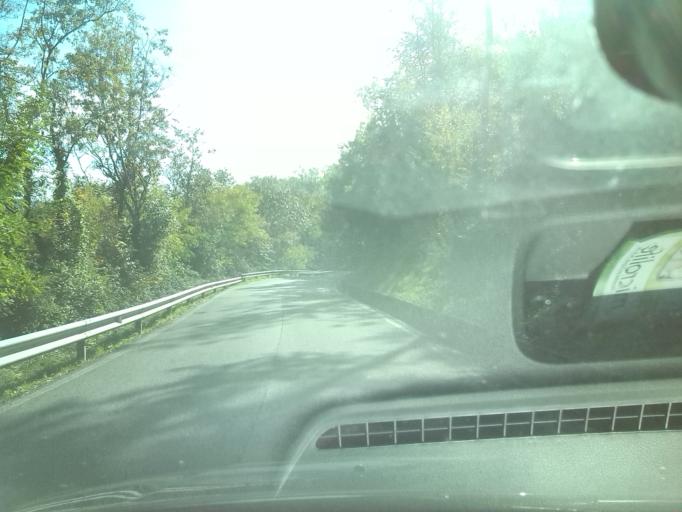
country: IT
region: Friuli Venezia Giulia
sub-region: Provincia di Udine
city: San Pietro al Natisone
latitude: 46.0882
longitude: 13.4696
